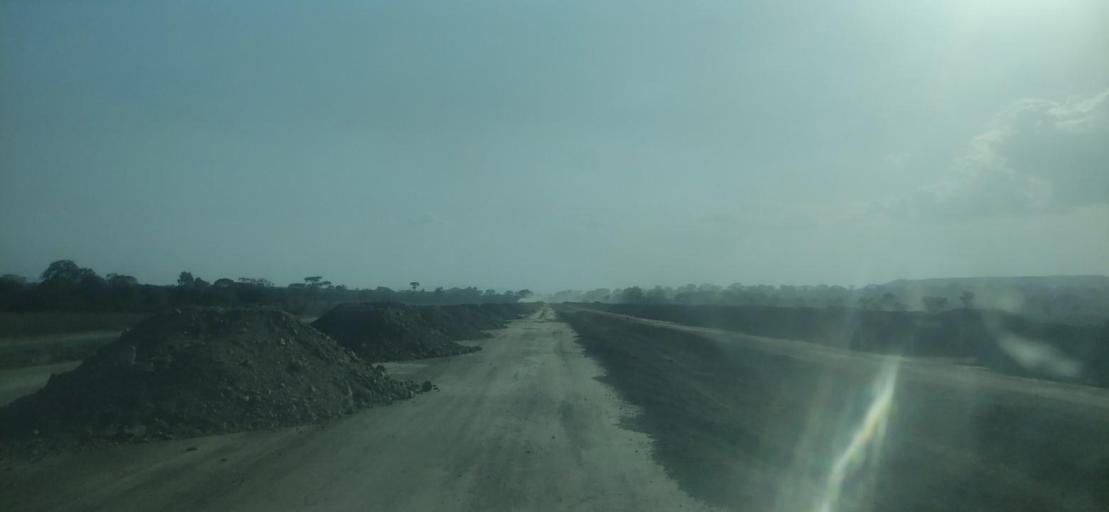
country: ET
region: Southern Nations, Nationalities, and People's Region
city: Hawassa
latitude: 7.1646
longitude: 38.4855
